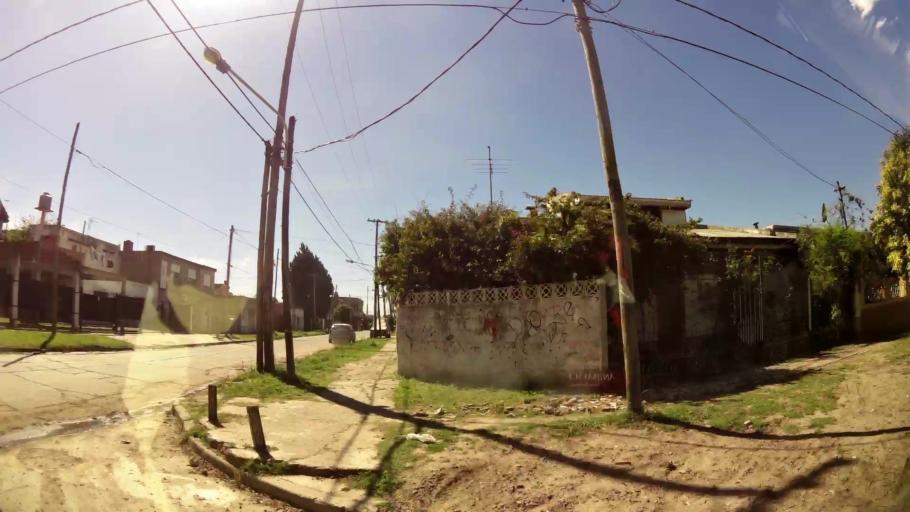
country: AR
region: Buenos Aires
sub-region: Partido de Almirante Brown
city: Adrogue
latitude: -34.7823
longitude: -58.3456
